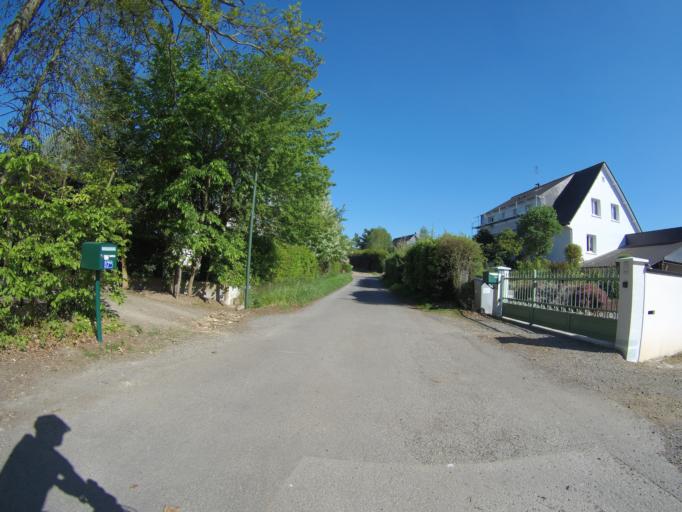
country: FR
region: Brittany
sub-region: Departement d'Ille-et-Vilaine
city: Vern-sur-Seiche
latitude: 48.0486
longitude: -1.6131
